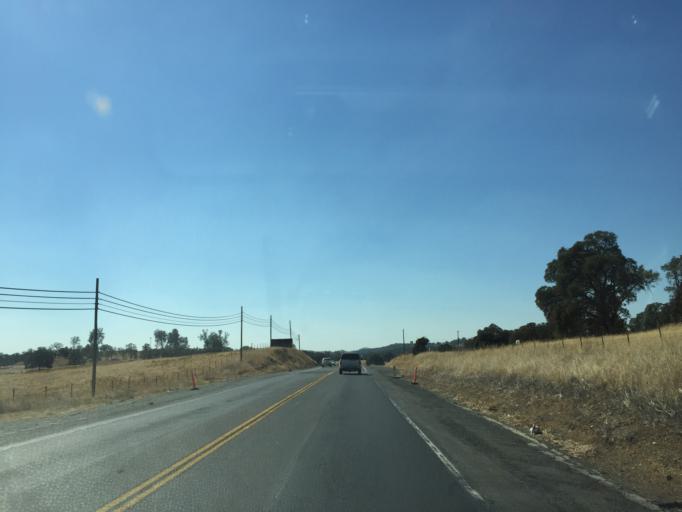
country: US
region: California
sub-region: Tuolumne County
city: Jamestown
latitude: 37.9282
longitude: -120.4456
